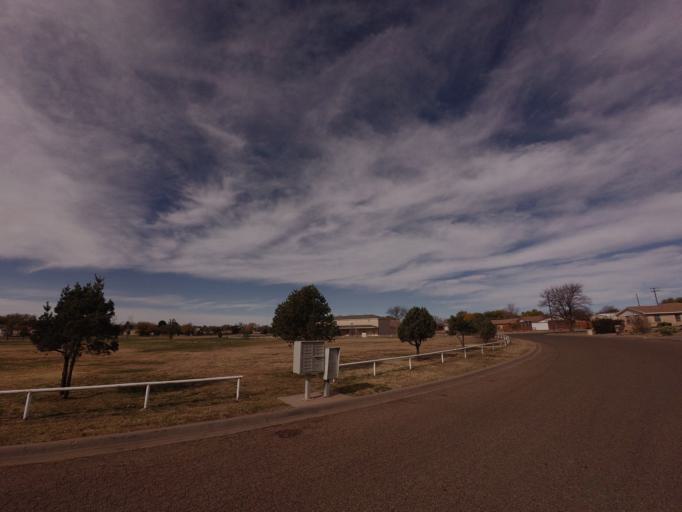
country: US
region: New Mexico
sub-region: Curry County
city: Clovis
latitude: 34.4124
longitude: -103.1913
